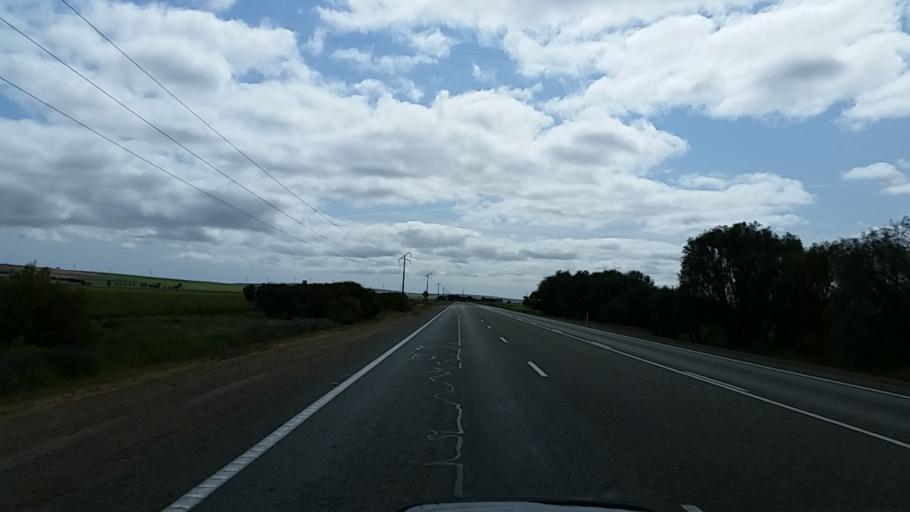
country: AU
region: South Australia
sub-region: Port Pirie City and Dists
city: Crystal Brook
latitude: -33.5257
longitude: 138.2015
